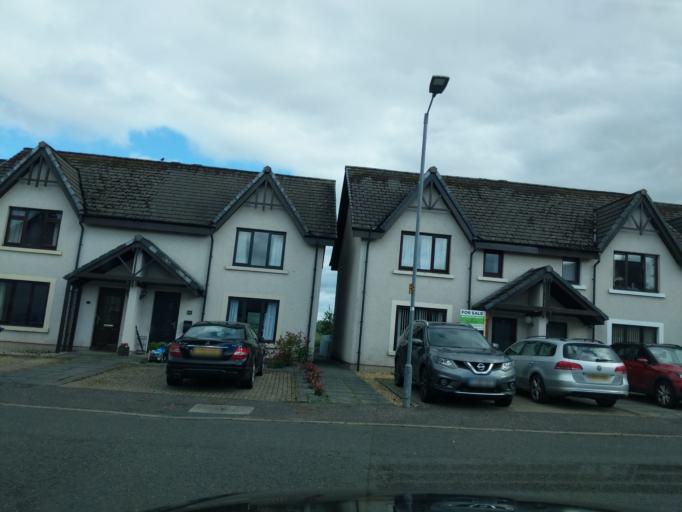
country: GB
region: Scotland
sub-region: The Scottish Borders
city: West Linton
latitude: 55.7514
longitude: -3.3515
